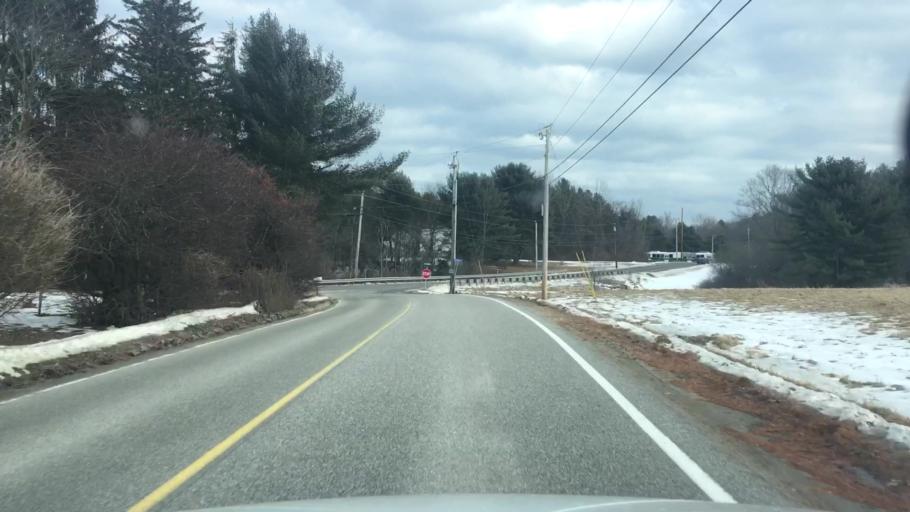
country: US
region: Maine
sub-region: York County
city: Arundel
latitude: 43.4079
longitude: -70.4931
